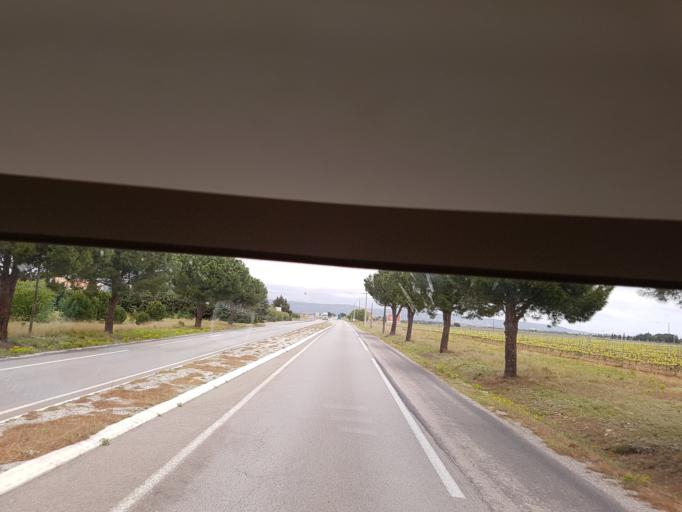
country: FR
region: Languedoc-Roussillon
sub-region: Departement des Pyrenees-Orientales
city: Salses-le-Chateau
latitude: 42.7970
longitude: 2.9090
